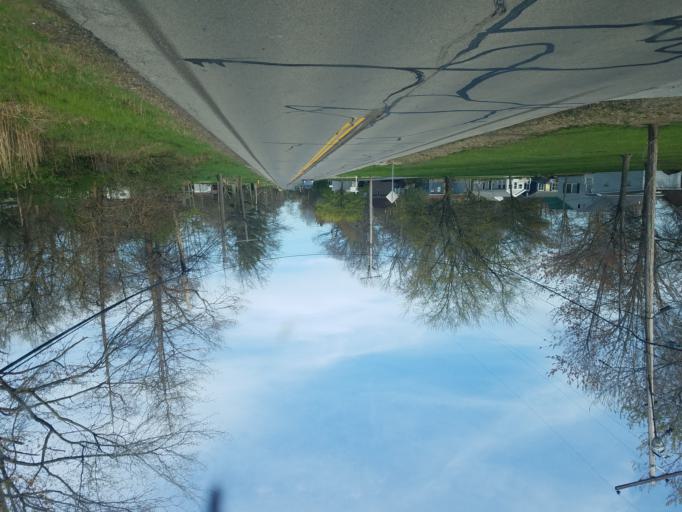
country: US
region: Ohio
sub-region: Ashtabula County
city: Geneva-on-the-Lake
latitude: 41.8765
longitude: -80.8739
